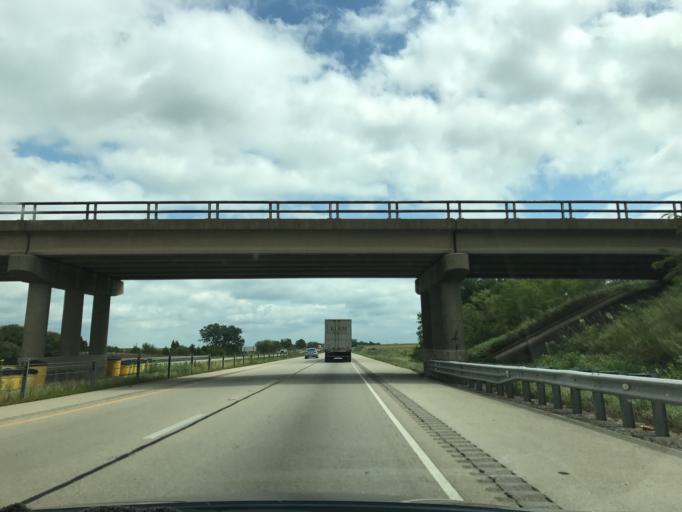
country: US
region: Illinois
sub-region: LaSalle County
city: Marseilles
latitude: 41.3754
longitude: -88.6721
